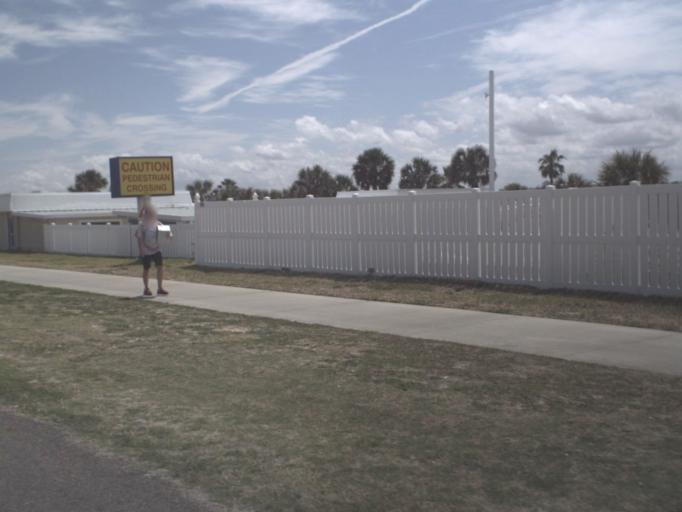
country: US
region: Florida
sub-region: Flagler County
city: Flagler Beach
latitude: 29.5223
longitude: -81.1483
